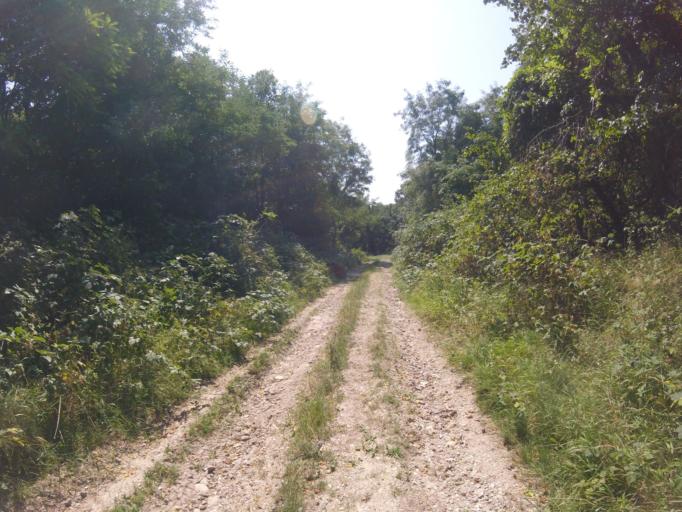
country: HU
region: Pest
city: Csobanka
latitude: 47.6887
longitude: 18.9580
